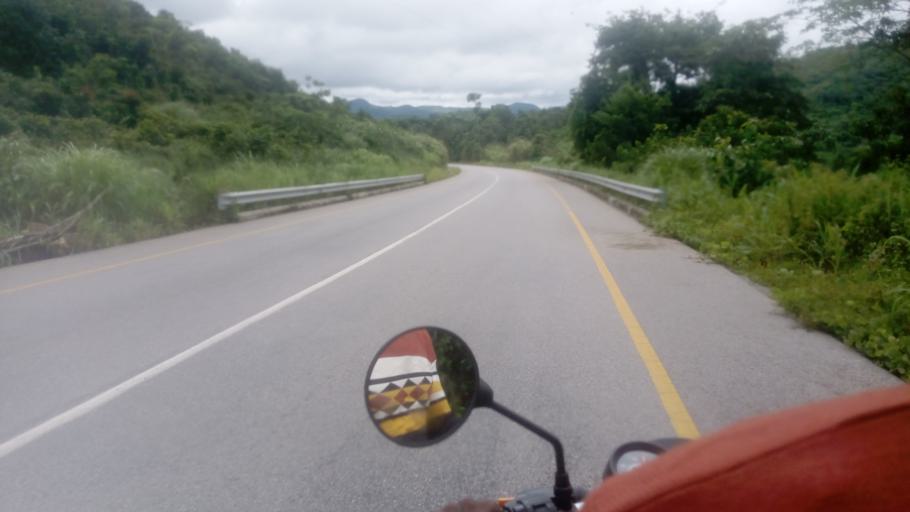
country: SL
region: Northern Province
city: Masaka
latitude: 8.6452
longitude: -11.7555
